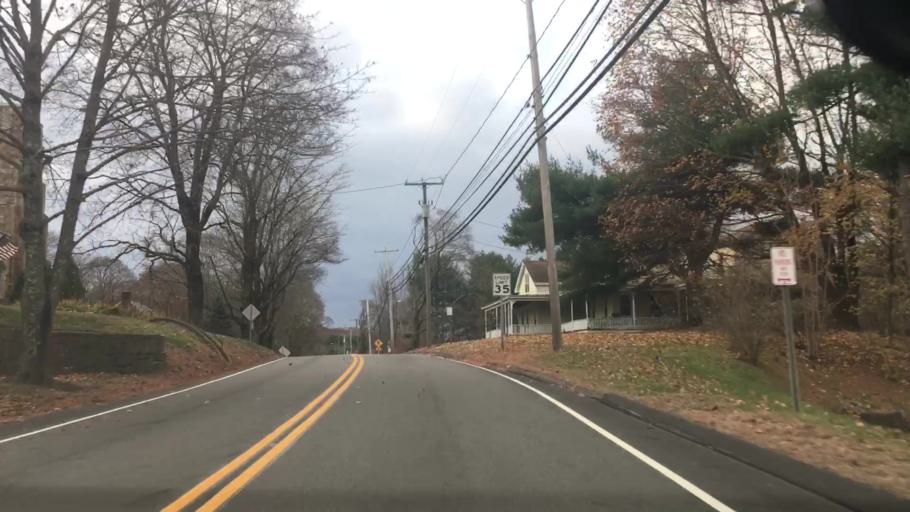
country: US
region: Connecticut
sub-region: Tolland County
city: Storrs
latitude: 41.8545
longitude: -72.3010
